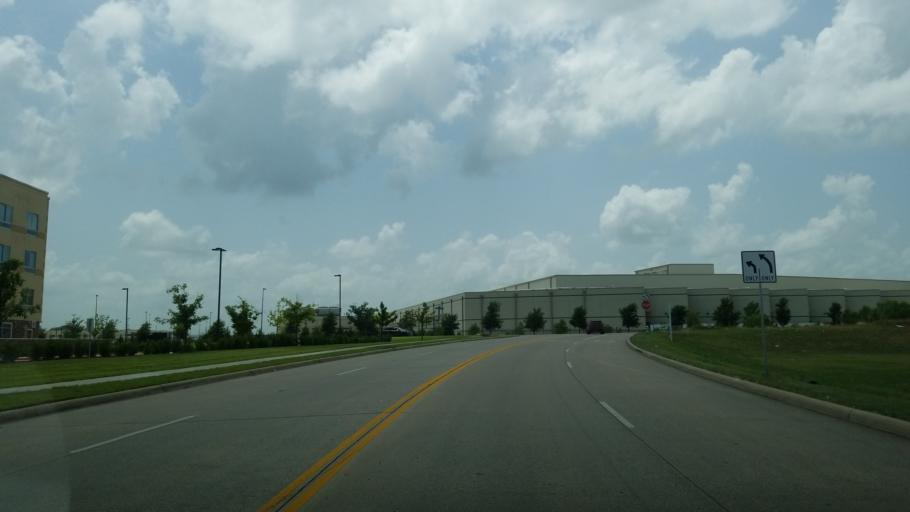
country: US
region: Texas
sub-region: Dallas County
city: Cockrell Hill
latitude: 32.7711
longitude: -96.8953
